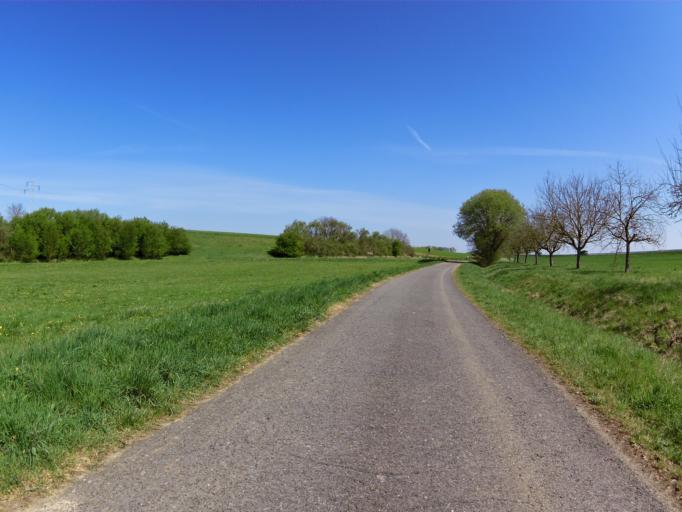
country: DE
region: Bavaria
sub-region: Regierungsbezirk Unterfranken
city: Kurnach
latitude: 49.8589
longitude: 10.0244
